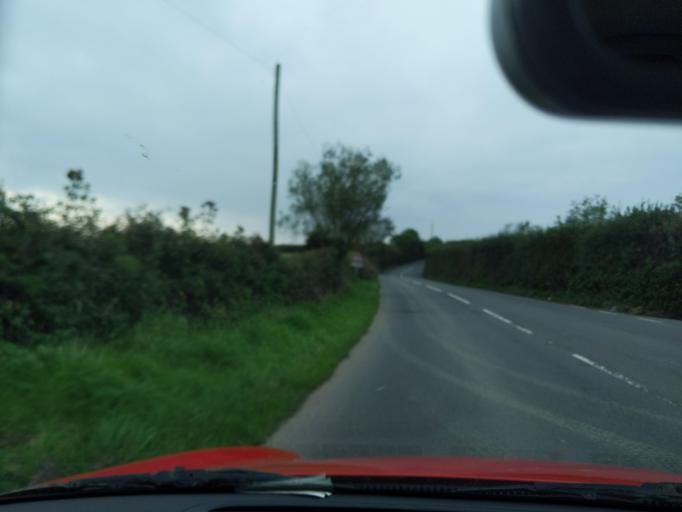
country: GB
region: England
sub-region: Devon
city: Winkleigh
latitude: 50.8592
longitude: -4.0645
